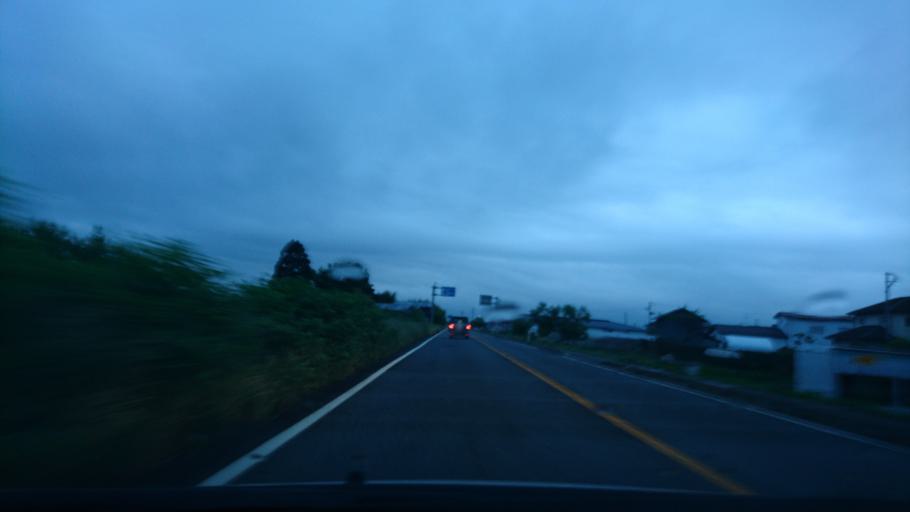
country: JP
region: Iwate
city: Ichinoseki
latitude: 38.8151
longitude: 141.0770
